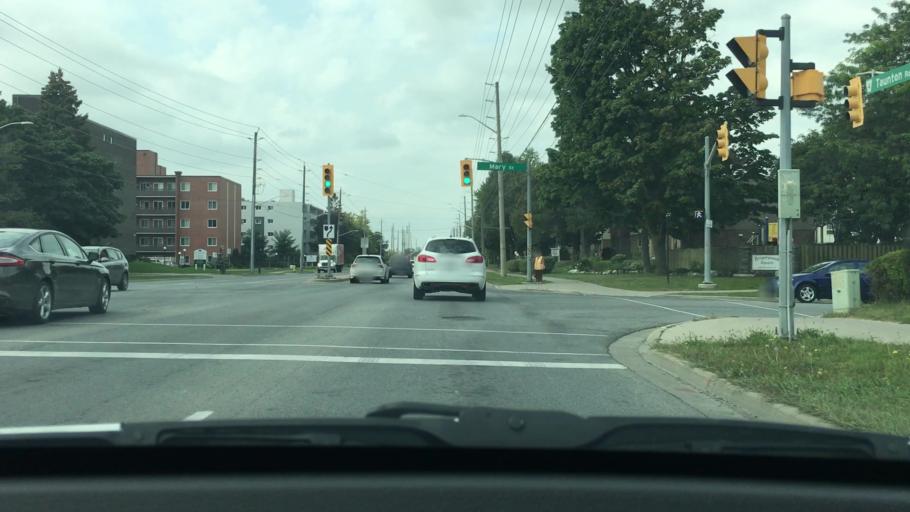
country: CA
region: Ontario
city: Oshawa
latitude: 43.9344
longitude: -78.8727
